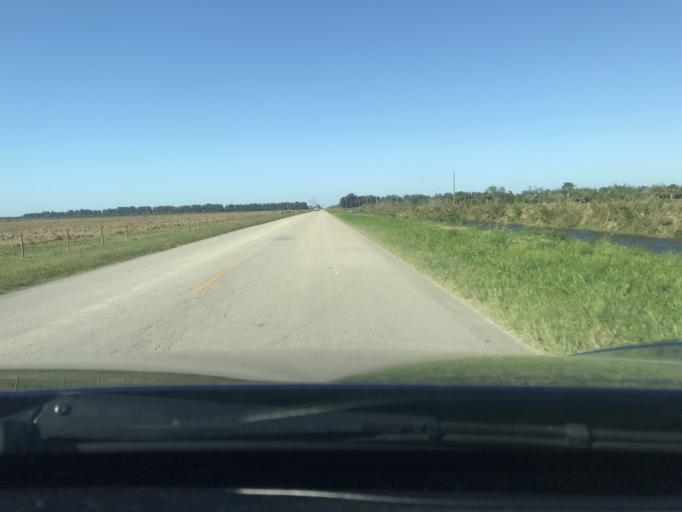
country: US
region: Florida
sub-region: Saint Lucie County
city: Lakewood Park
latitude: 27.4148
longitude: -80.4975
